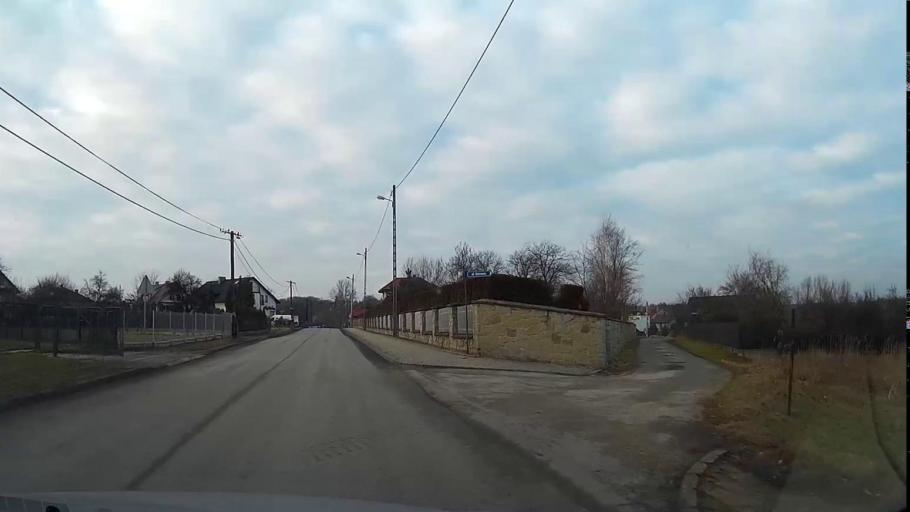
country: PL
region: Lesser Poland Voivodeship
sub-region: Powiat chrzanowski
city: Alwernia
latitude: 50.0645
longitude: 19.5456
